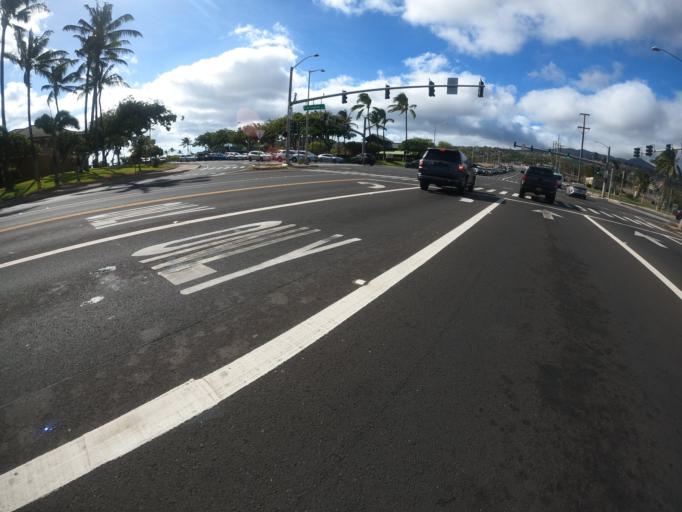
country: US
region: Hawaii
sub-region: Honolulu County
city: Makakilo City
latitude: 21.3399
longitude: -158.0758
